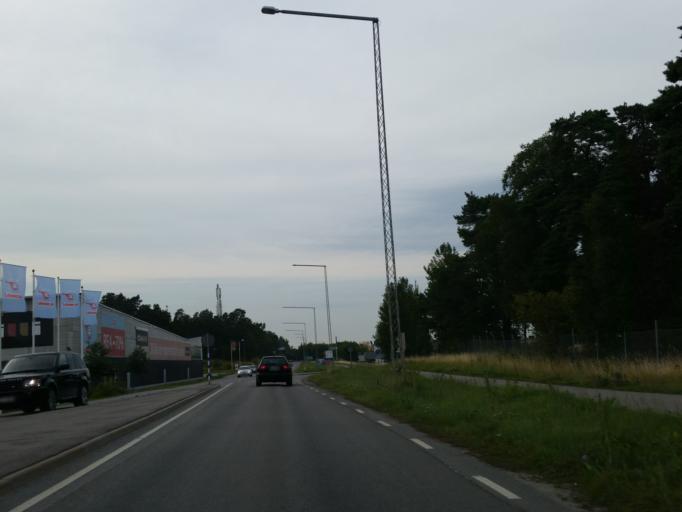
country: SE
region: Stockholm
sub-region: Jarfalla Kommun
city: Jakobsberg
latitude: 59.4145
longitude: 17.8572
